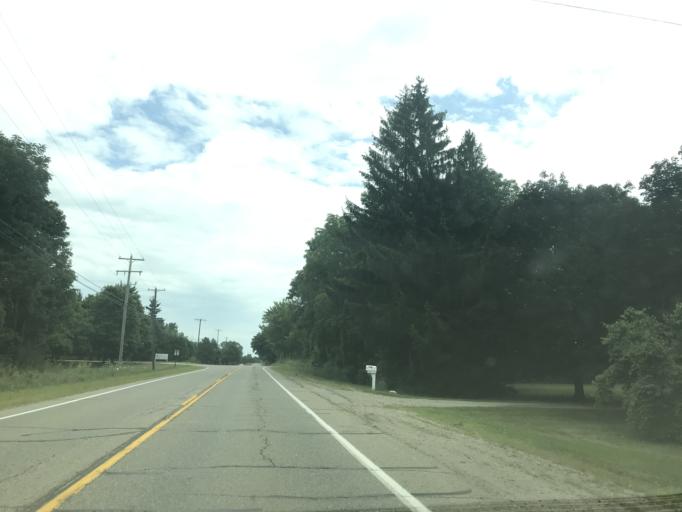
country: US
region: Michigan
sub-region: Clinton County
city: Wacousta
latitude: 42.7901
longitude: -84.6967
